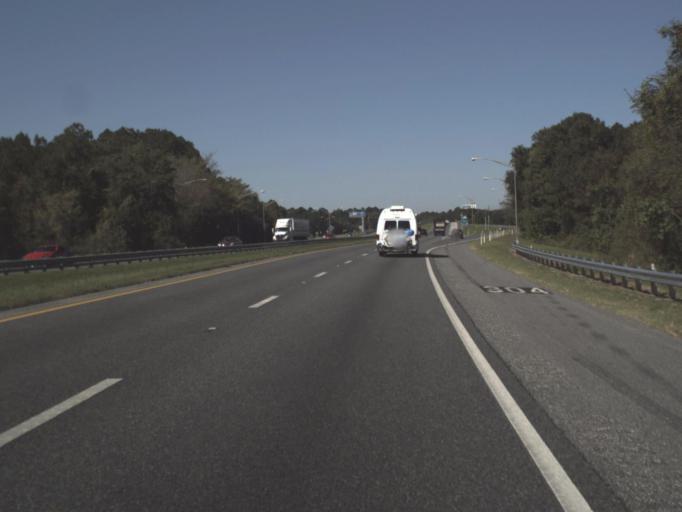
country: US
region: Florida
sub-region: Sumter County
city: Wildwood
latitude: 28.8343
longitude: -82.0403
